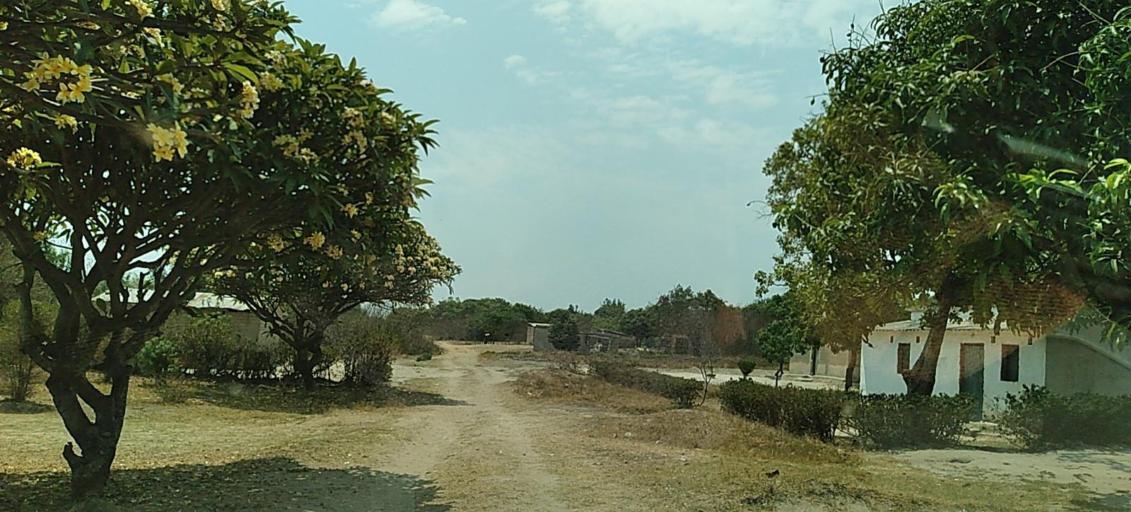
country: ZM
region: Copperbelt
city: Kalulushi
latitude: -12.9540
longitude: 28.1416
